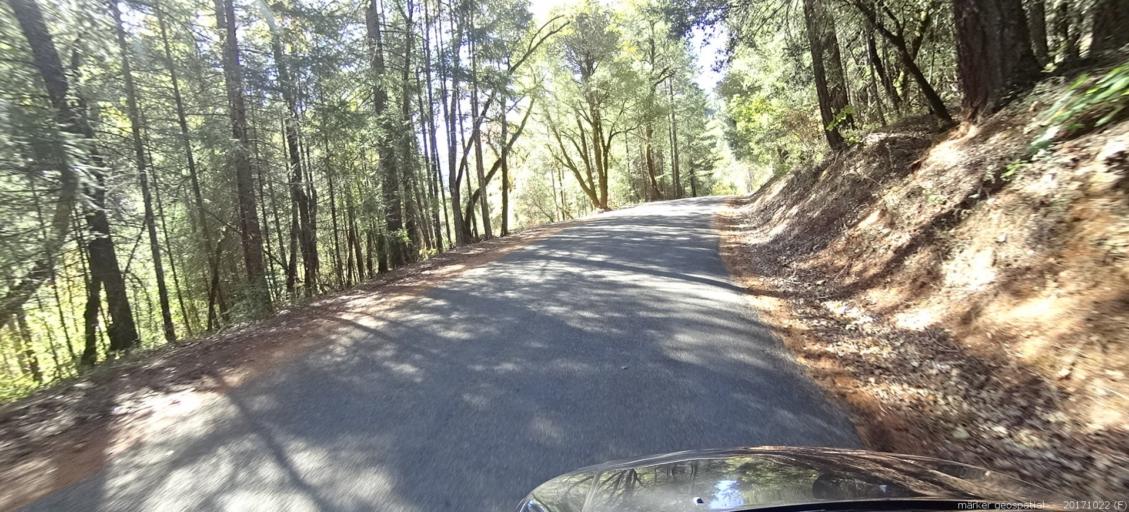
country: US
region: California
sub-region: Shasta County
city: Central Valley (historical)
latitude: 40.9335
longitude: -122.4619
